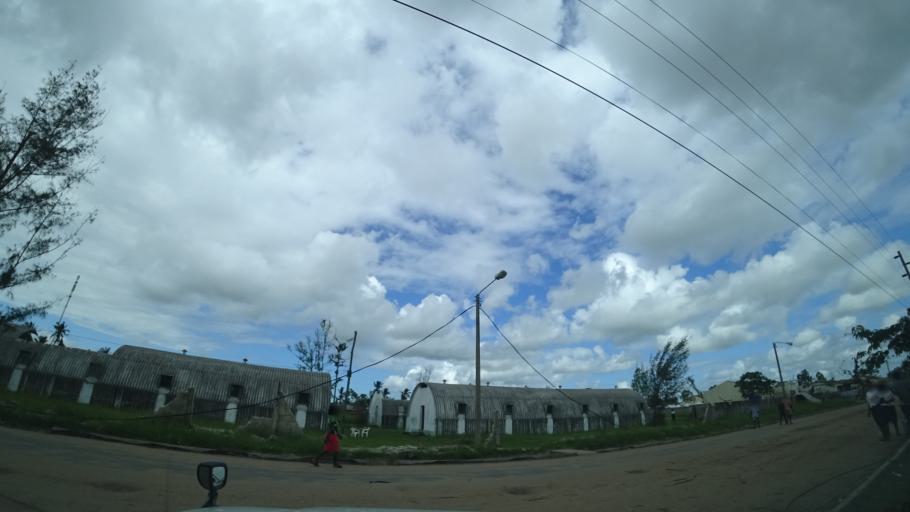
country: MZ
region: Sofala
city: Dondo
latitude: -19.6174
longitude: 34.7427
